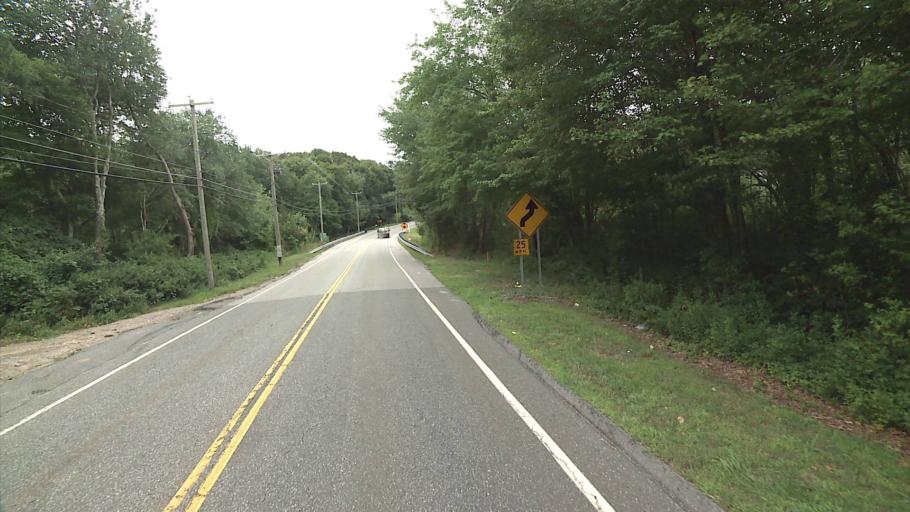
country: US
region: Connecticut
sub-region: New London County
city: Niantic
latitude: 41.3106
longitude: -72.2537
